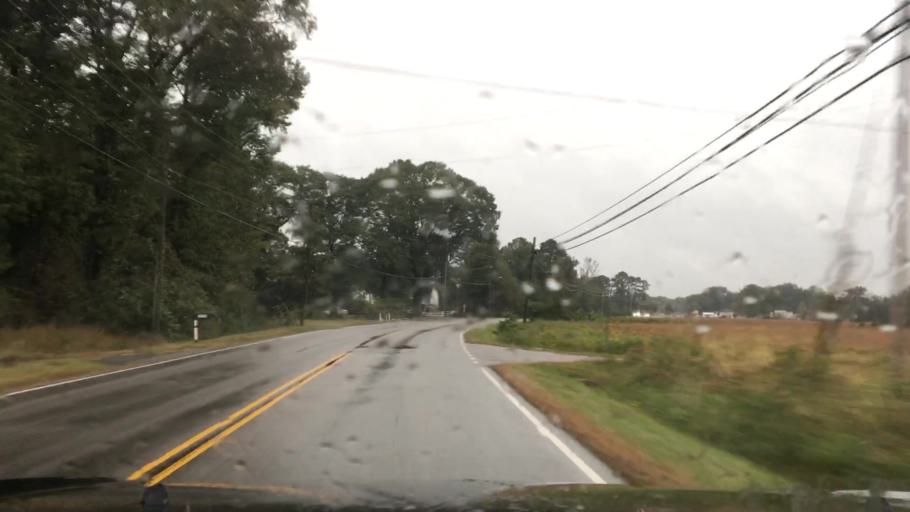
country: US
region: North Carolina
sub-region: Currituck County
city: Moyock
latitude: 36.6663
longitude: -76.2267
